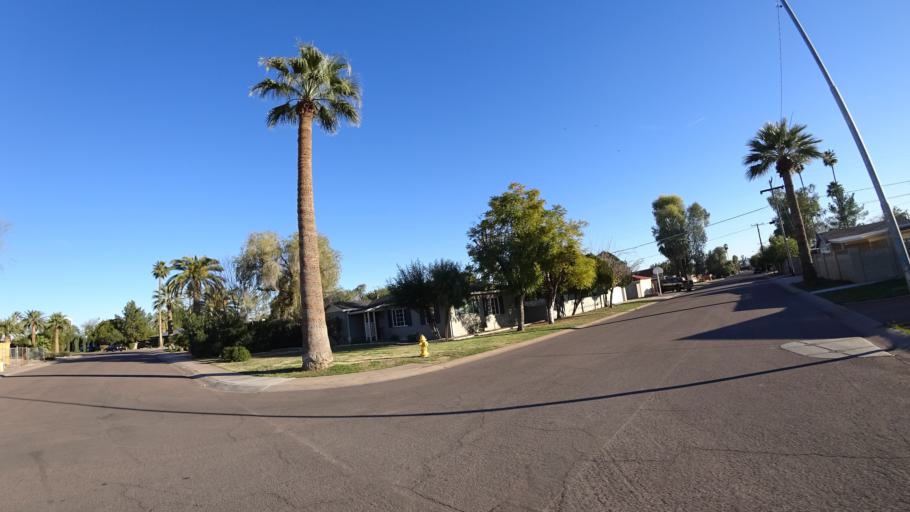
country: US
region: Arizona
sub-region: Maricopa County
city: Phoenix
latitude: 33.4850
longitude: -112.0936
